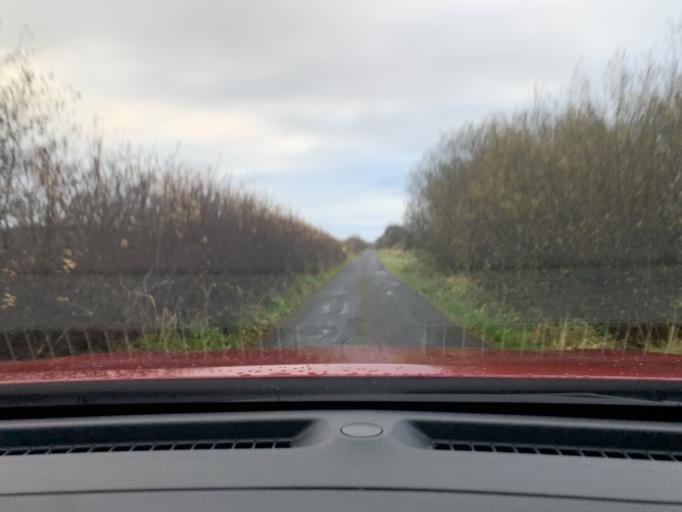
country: IE
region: Connaught
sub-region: Sligo
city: Ballymote
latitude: 54.0163
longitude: -8.5101
